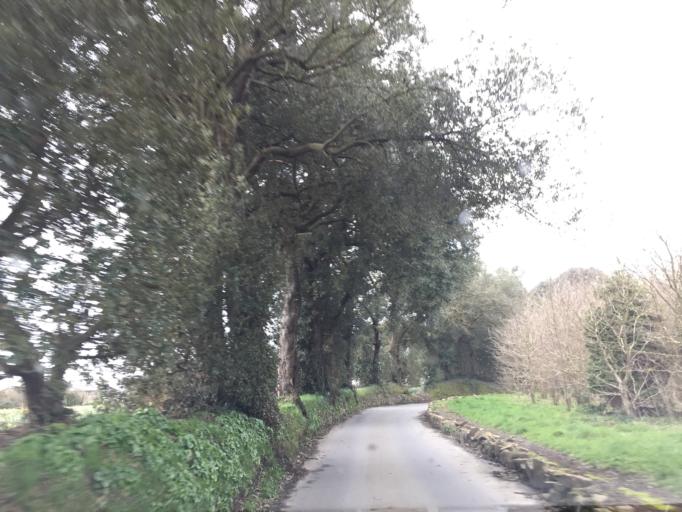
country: JE
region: St Helier
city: Saint Helier
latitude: 49.2067
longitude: -2.1471
